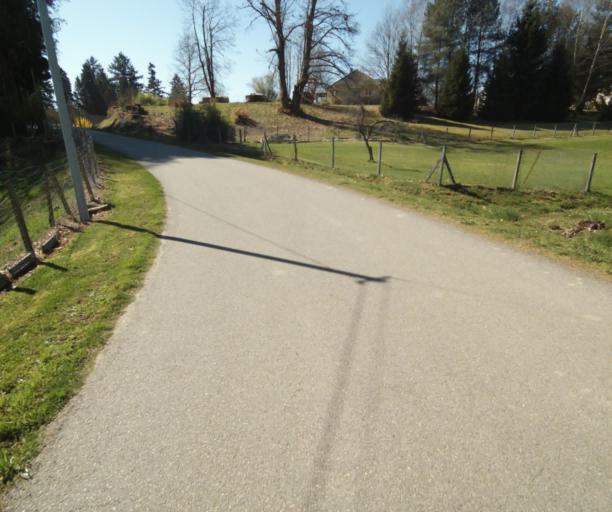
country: FR
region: Limousin
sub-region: Departement de la Correze
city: Saint-Clement
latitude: 45.3028
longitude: 1.7008
